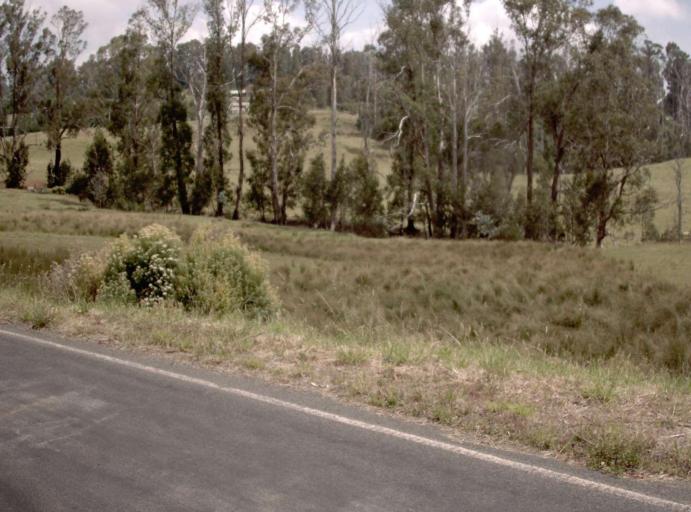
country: AU
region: Victoria
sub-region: Latrobe
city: Traralgon
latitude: -38.3275
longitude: 146.5742
